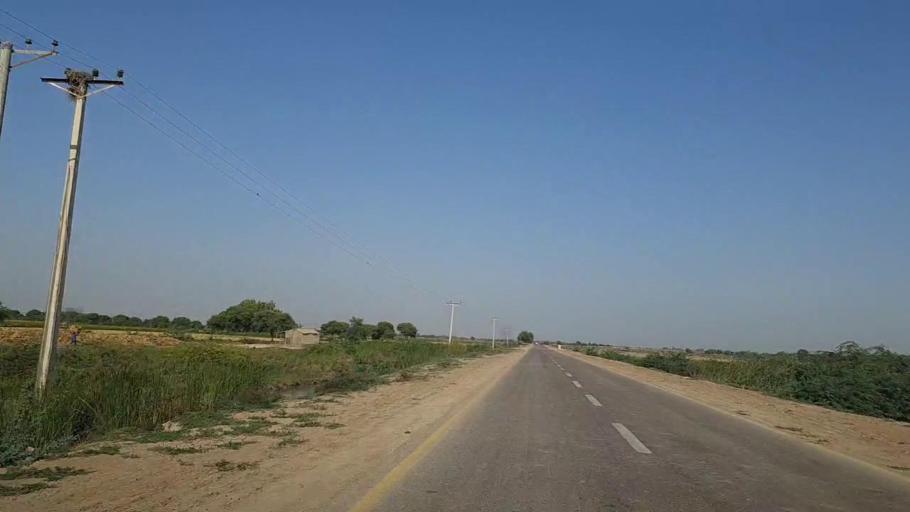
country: PK
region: Sindh
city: Jati
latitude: 24.4535
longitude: 68.3398
